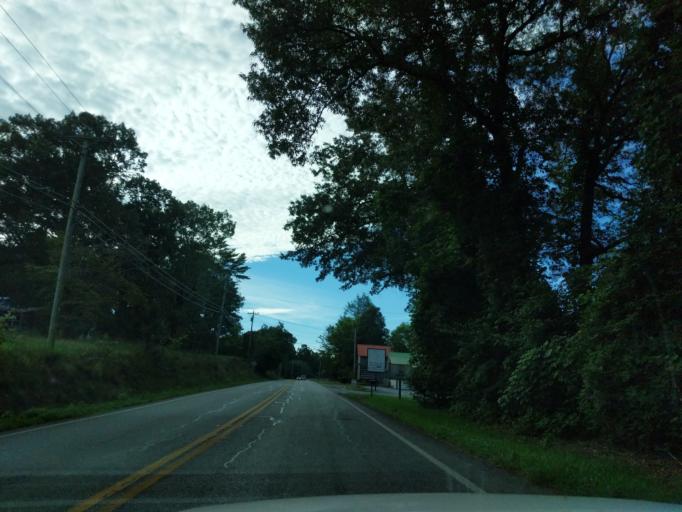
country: US
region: Georgia
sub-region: Fannin County
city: McCaysville
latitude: 34.9614
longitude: -84.3711
